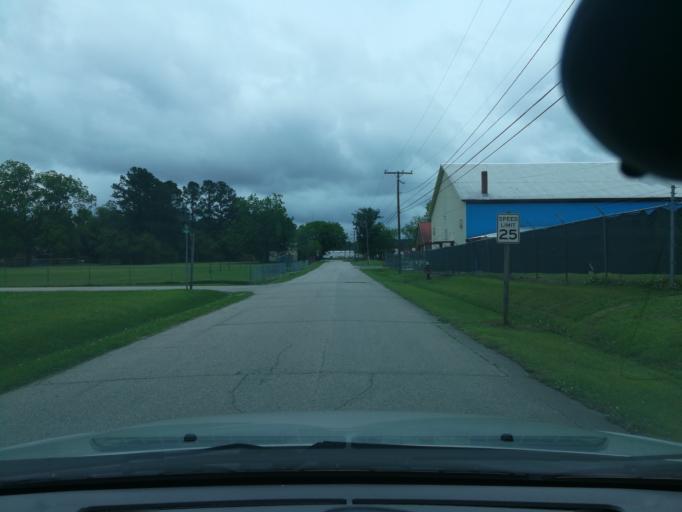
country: US
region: North Carolina
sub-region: Washington County
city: Plymouth
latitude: 35.8629
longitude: -76.7466
